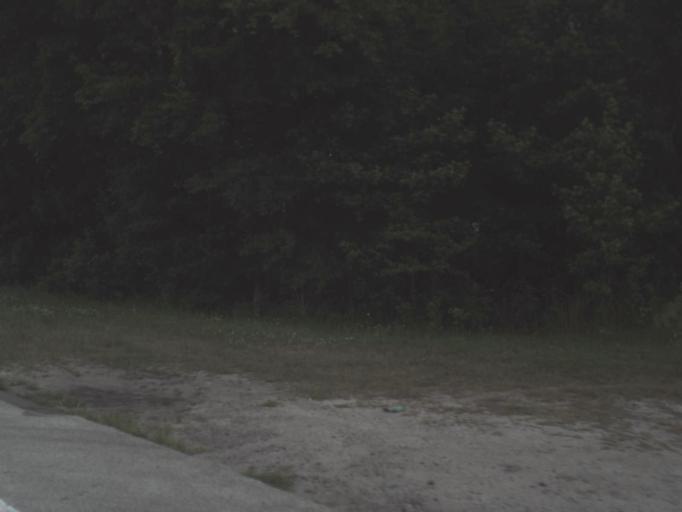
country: US
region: Florida
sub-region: Saint Johns County
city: Saint Augustine Shores
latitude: 29.7261
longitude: -81.4248
